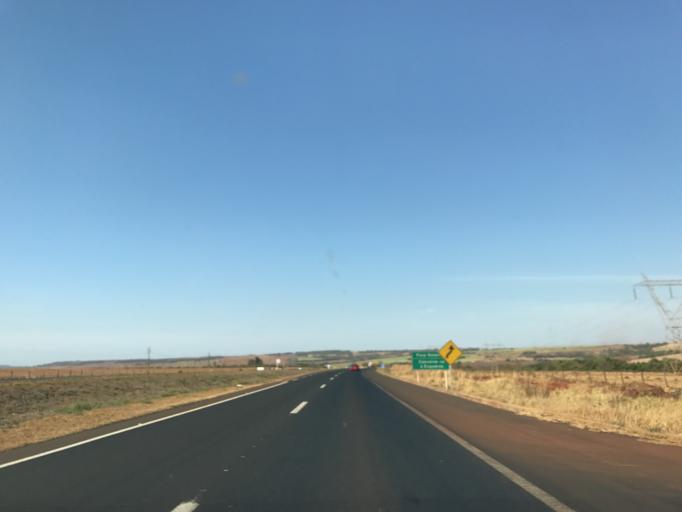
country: BR
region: Goias
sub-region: Goiatuba
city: Goiatuba
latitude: -17.9827
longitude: -49.2576
